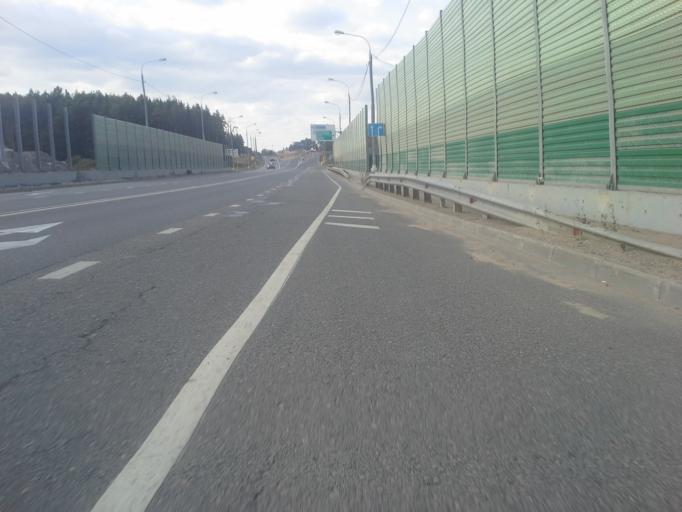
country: RU
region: Moskovskaya
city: Golitsyno
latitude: 55.5987
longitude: 37.0076
